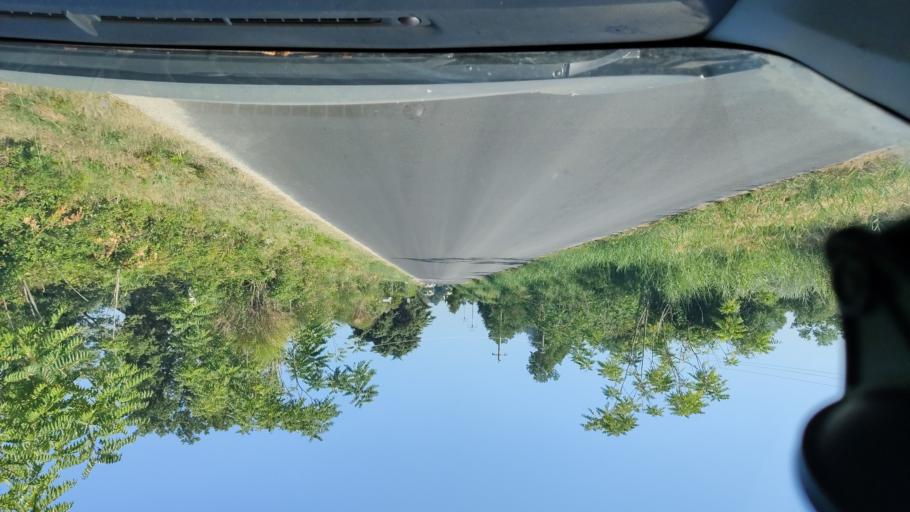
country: IT
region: Umbria
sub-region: Provincia di Terni
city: Fornole
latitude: 42.5235
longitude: 12.4342
